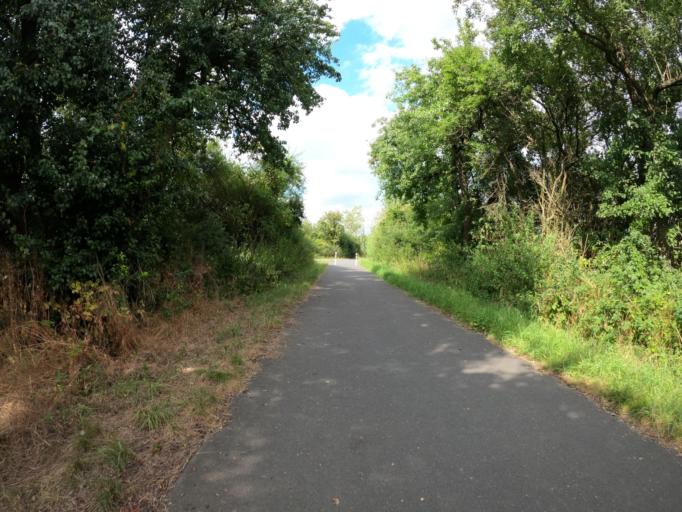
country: DE
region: Mecklenburg-Vorpommern
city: Woldegk
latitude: 53.3850
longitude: 13.5895
